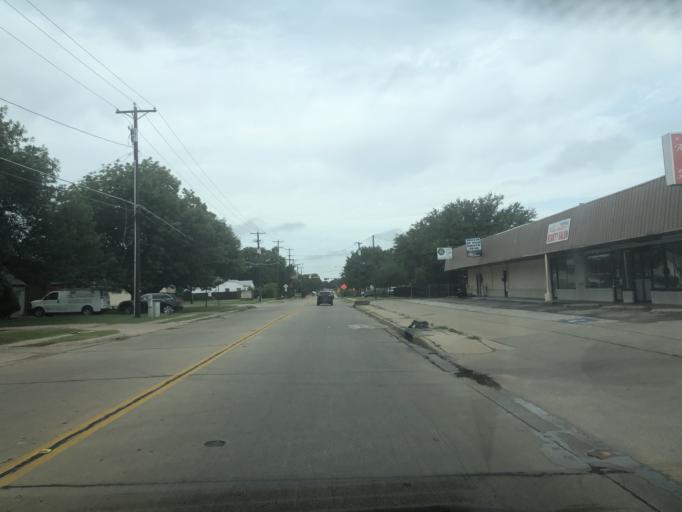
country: US
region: Texas
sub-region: Dallas County
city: Irving
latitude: 32.8086
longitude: -96.9482
